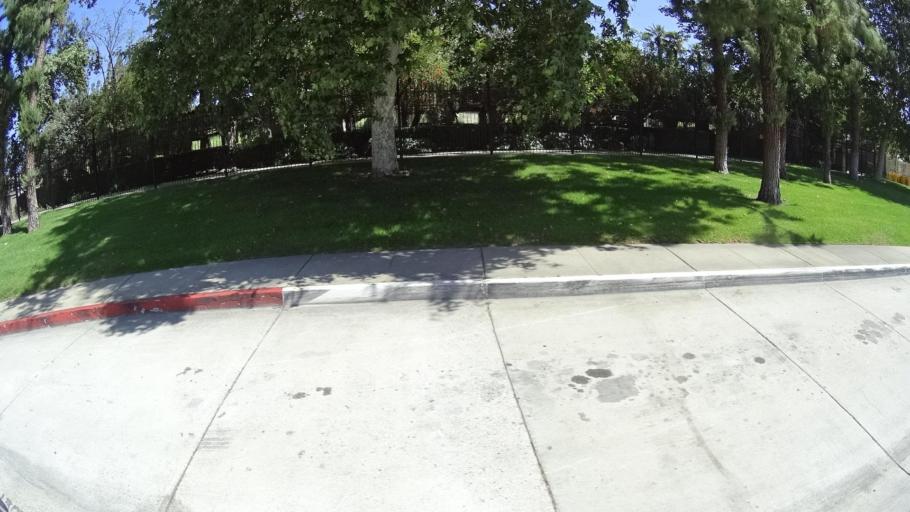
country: US
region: California
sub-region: Los Angeles County
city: La Puente
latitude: 34.0197
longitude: -117.9660
